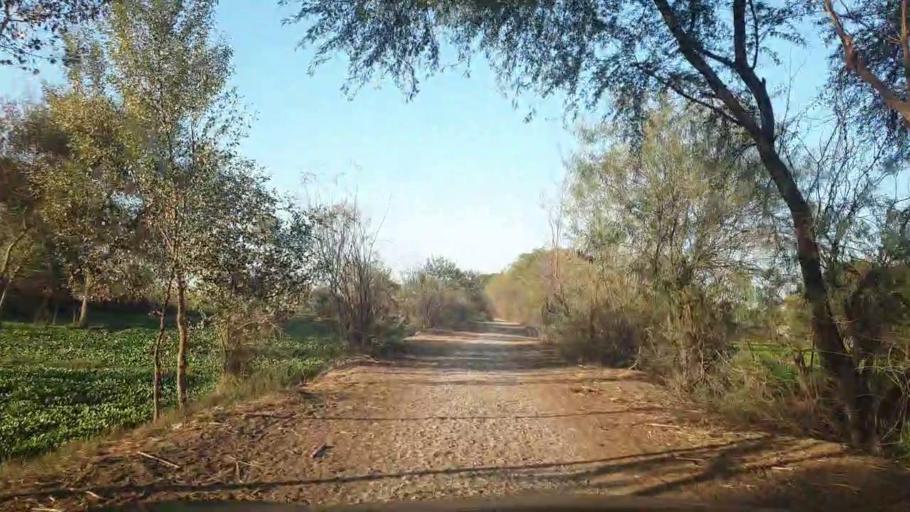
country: PK
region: Sindh
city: Mirpur Mathelo
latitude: 28.0077
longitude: 69.4612
